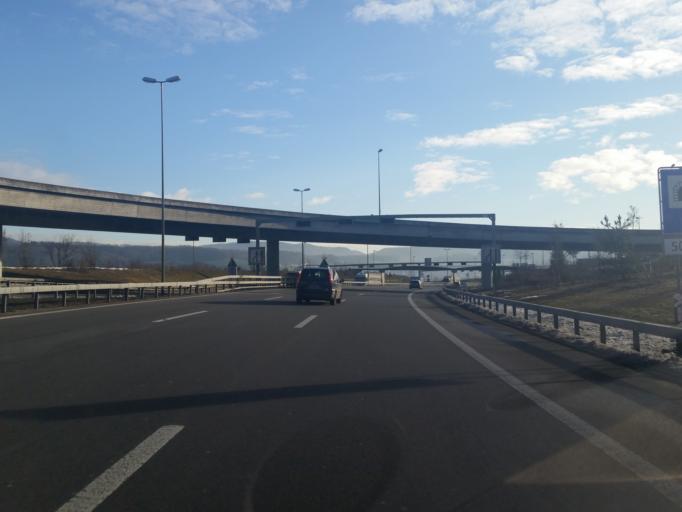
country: CH
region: Zurich
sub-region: Bezirk Affoltern
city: Wettswil / Wettswil (Dorf)
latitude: 47.3392
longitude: 8.4591
